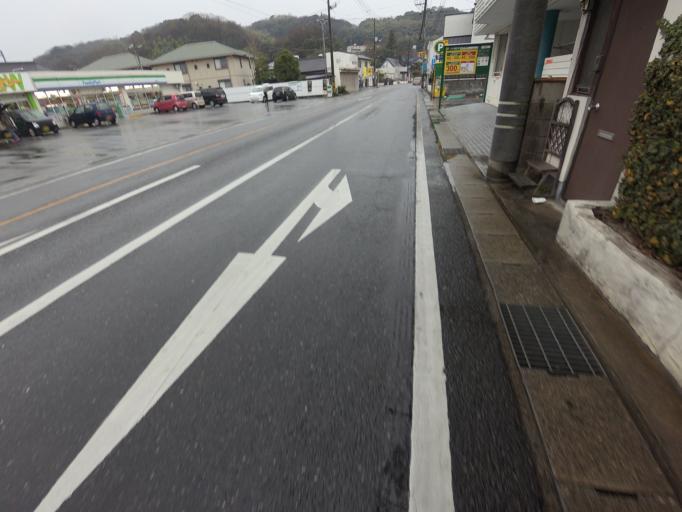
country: JP
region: Okayama
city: Kurashiki
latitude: 34.5962
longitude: 133.7776
